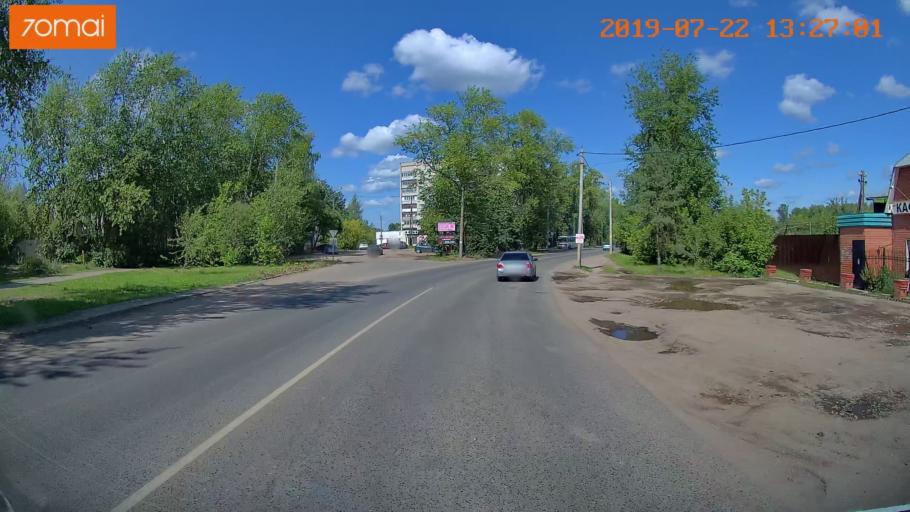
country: RU
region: Ivanovo
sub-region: Gorod Ivanovo
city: Ivanovo
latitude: 57.0316
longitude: 40.9479
